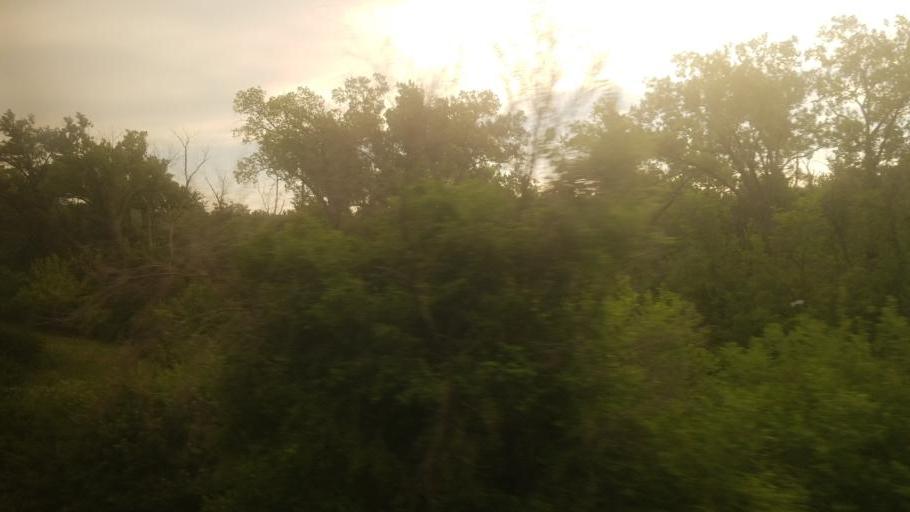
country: US
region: Kansas
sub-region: Shawnee County
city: Topeka
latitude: 38.9895
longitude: -95.6870
